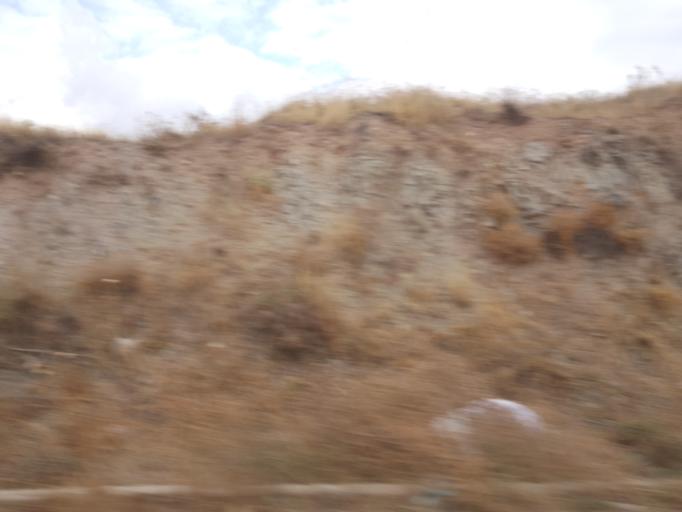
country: TR
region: Kirikkale
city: Keskin
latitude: 39.6740
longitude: 33.6040
